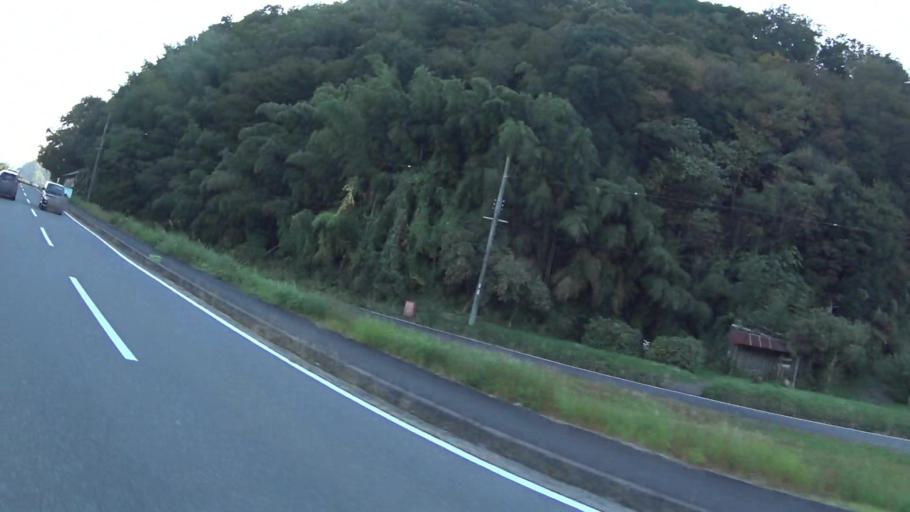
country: JP
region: Kyoto
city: Fukuchiyama
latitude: 35.3271
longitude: 135.1108
